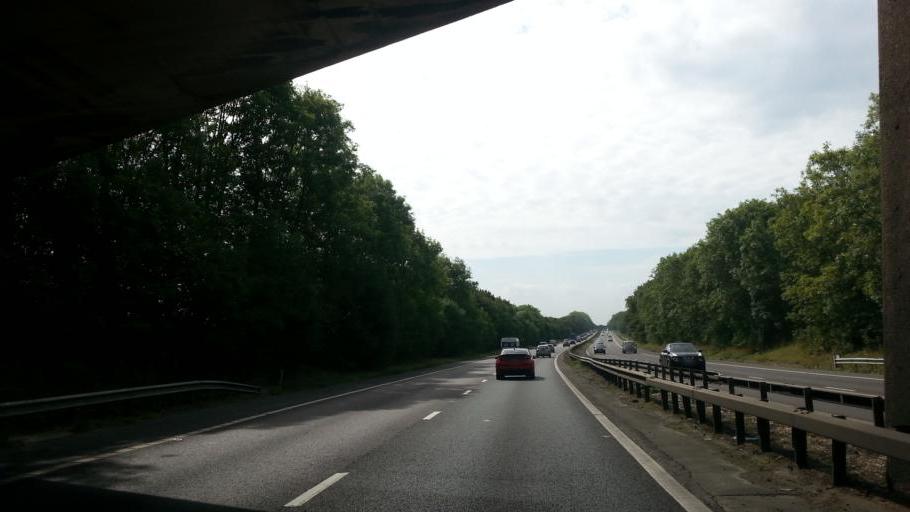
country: GB
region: England
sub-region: Hertfordshire
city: Knebworth
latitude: 51.8669
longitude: -0.1972
